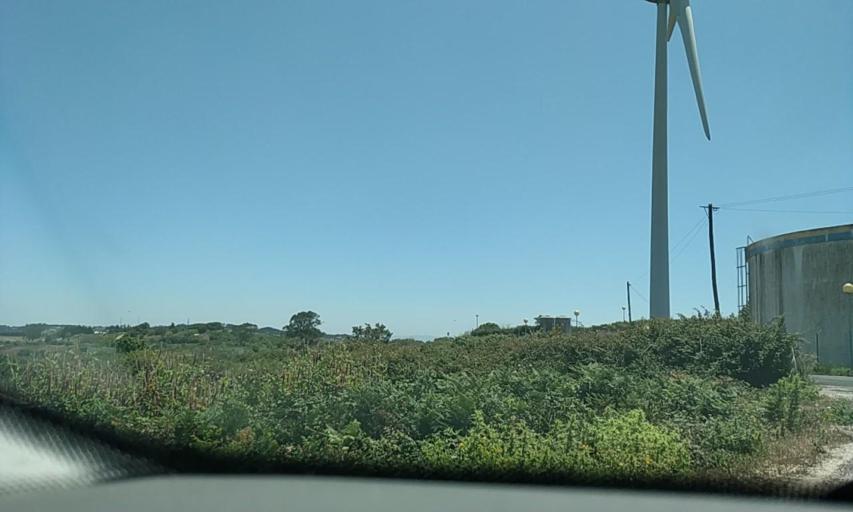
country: PT
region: Lisbon
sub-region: Sintra
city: Almargem
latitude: 38.8407
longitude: -9.2681
